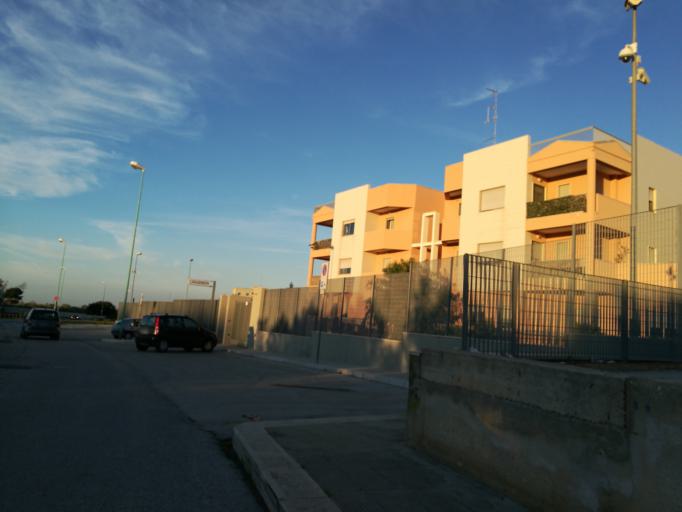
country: IT
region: Apulia
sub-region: Provincia di Bari
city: Adelfia
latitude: 41.0059
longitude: 16.8742
